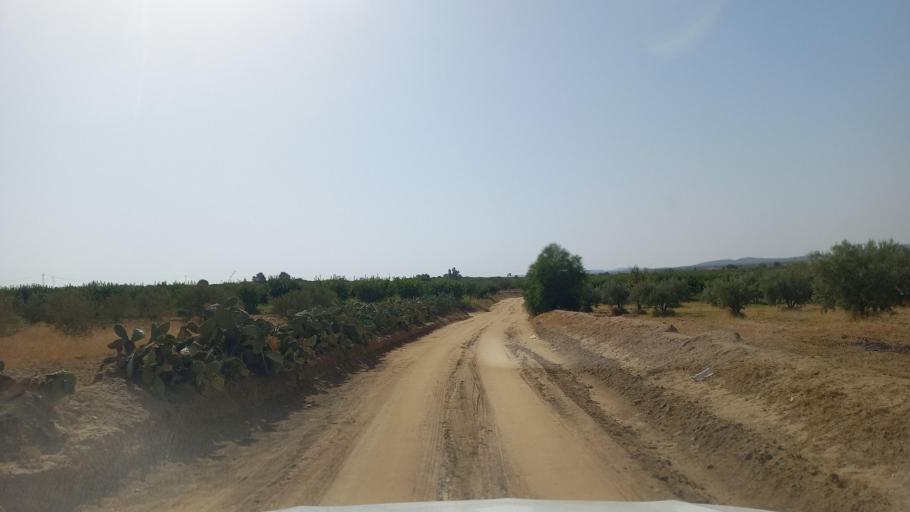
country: TN
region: Al Qasrayn
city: Kasserine
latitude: 35.2441
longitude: 9.0336
